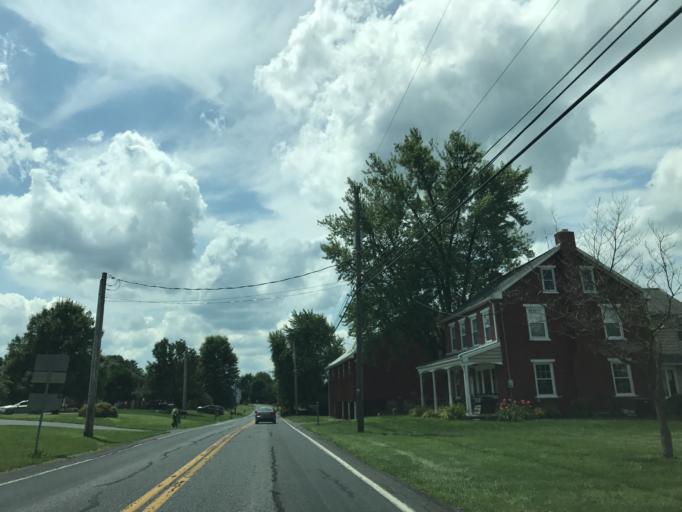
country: US
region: Pennsylvania
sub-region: Lancaster County
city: Penryn
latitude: 40.2061
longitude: -76.3446
